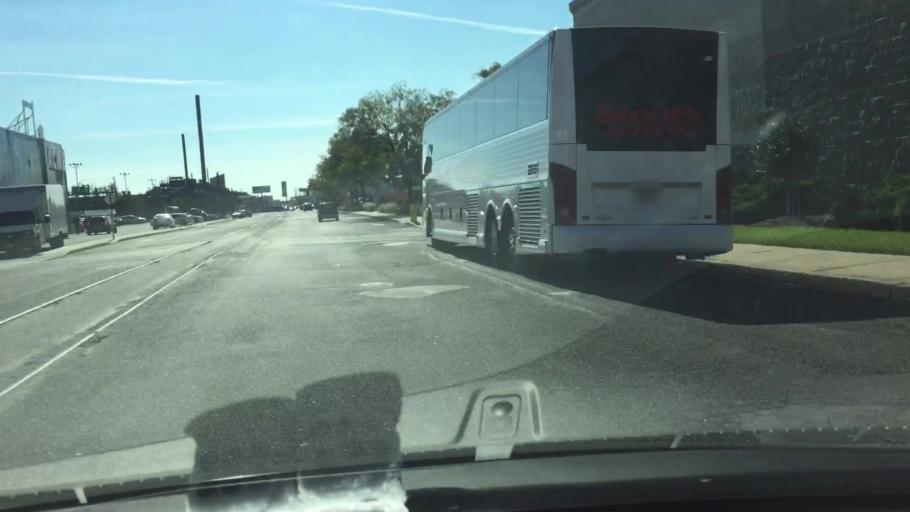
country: US
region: New Jersey
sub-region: Camden County
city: Camden
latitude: 39.9241
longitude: -75.1456
